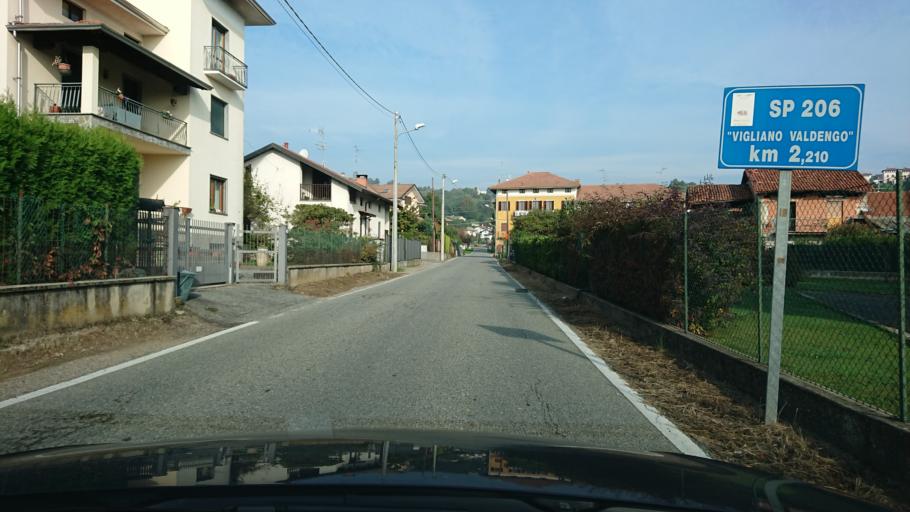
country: IT
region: Piedmont
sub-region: Provincia di Biella
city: Valdengo
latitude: 45.5689
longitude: 8.1318
